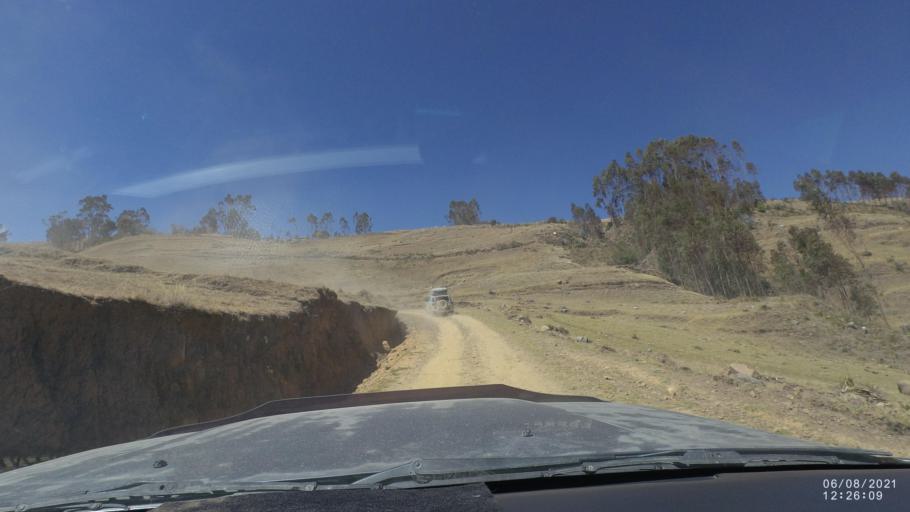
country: BO
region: Cochabamba
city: Colchani
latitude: -16.7931
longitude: -66.6556
